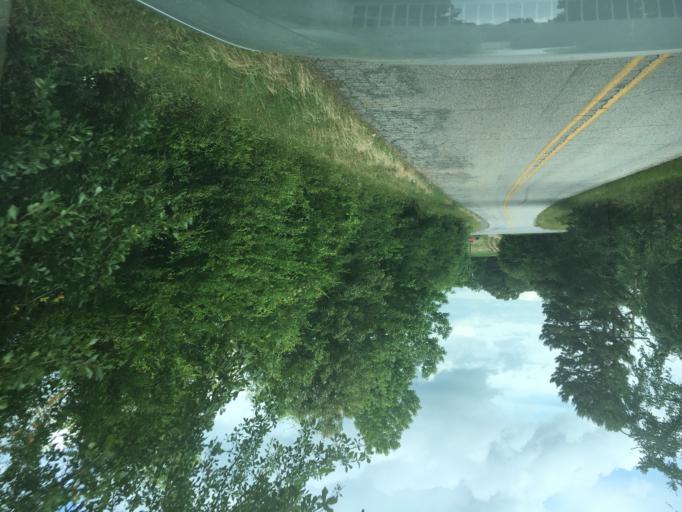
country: US
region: South Carolina
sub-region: Laurens County
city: Watts Mills
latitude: 34.5310
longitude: -81.9655
